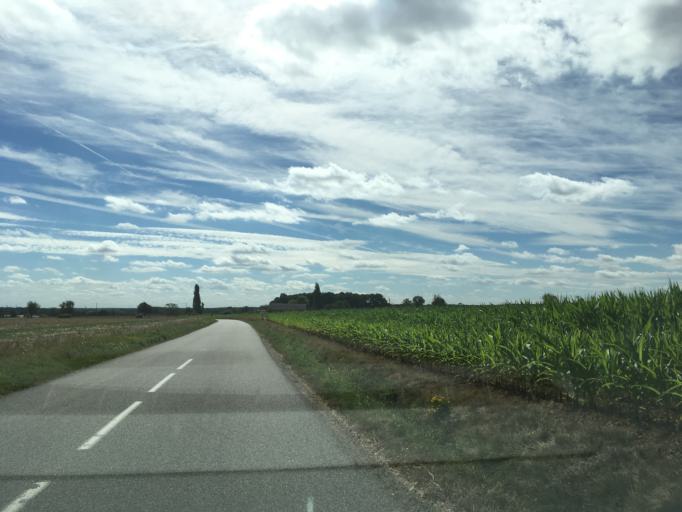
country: FR
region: Haute-Normandie
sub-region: Departement de l'Eure
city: Saint-Aubin-sur-Gaillon
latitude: 49.1373
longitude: 1.2817
